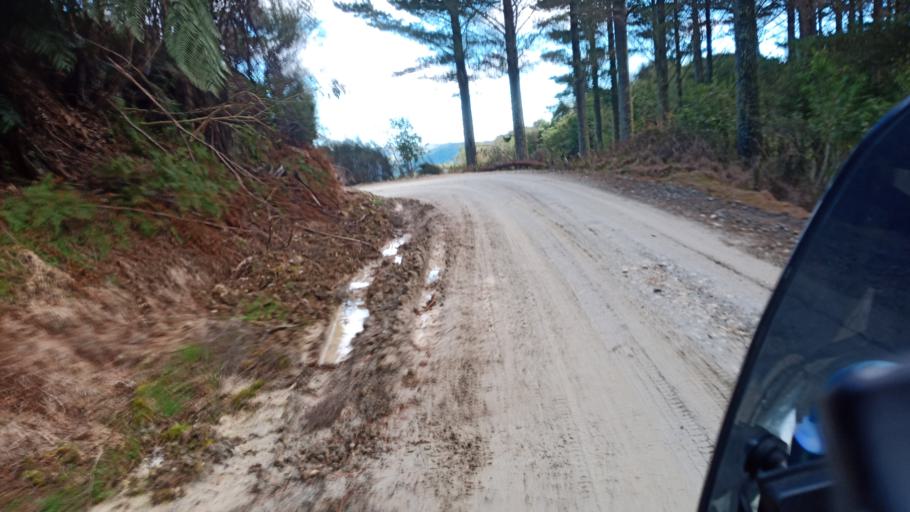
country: NZ
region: Gisborne
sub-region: Gisborne District
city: Gisborne
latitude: -38.8629
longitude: 177.7939
